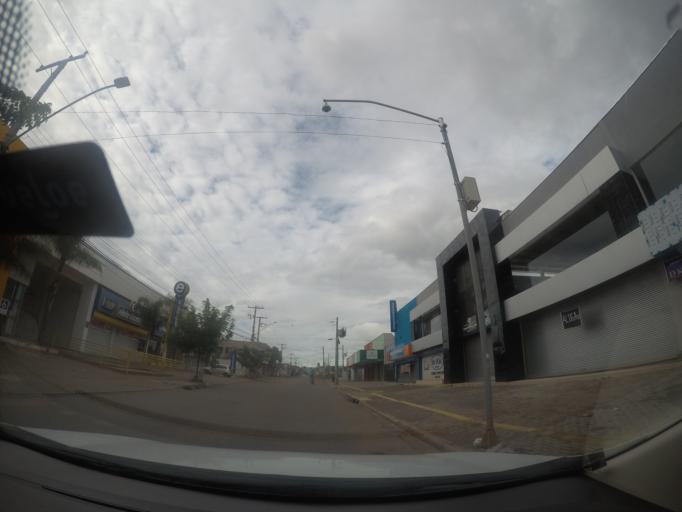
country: BR
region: Goias
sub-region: Goiania
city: Goiania
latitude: -16.6283
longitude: -49.3272
